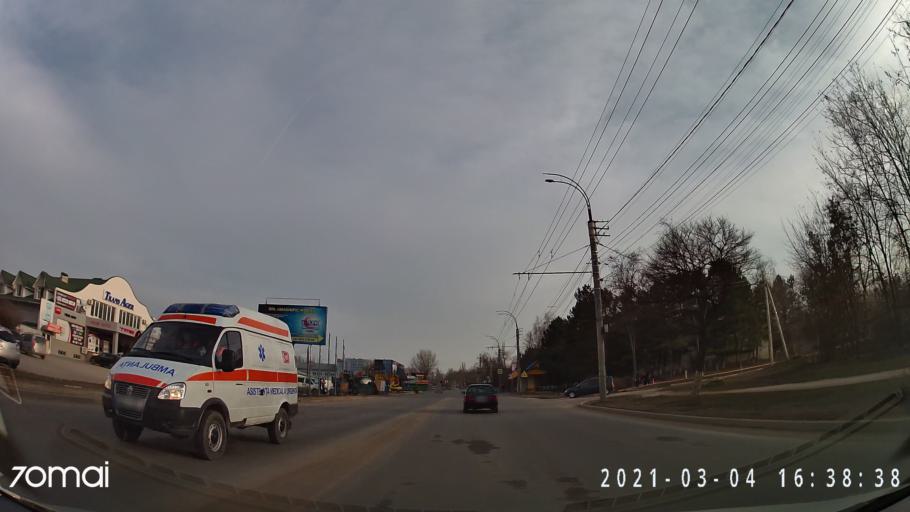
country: MD
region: Balti
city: Balti
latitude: 47.7798
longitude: 27.8919
